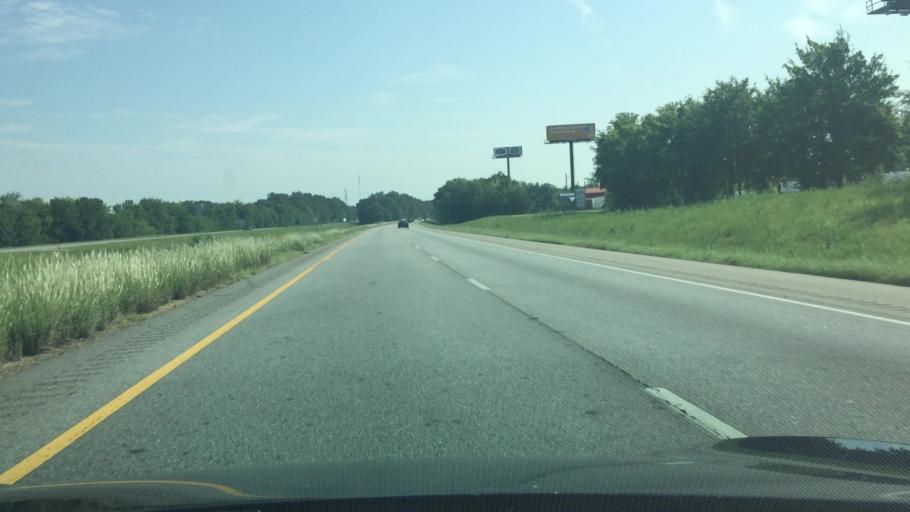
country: US
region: Alabama
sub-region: Lowndes County
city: Hayneville
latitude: 32.2051
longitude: -86.4115
